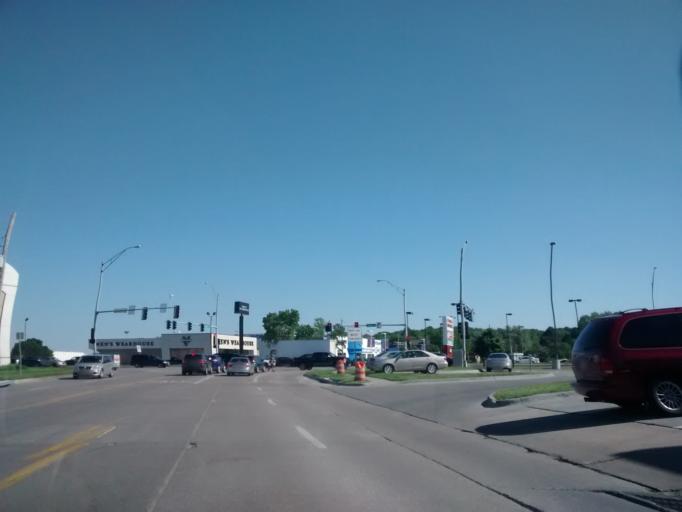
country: US
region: Nebraska
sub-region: Douglas County
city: Ralston
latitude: 41.2604
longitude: -96.0359
